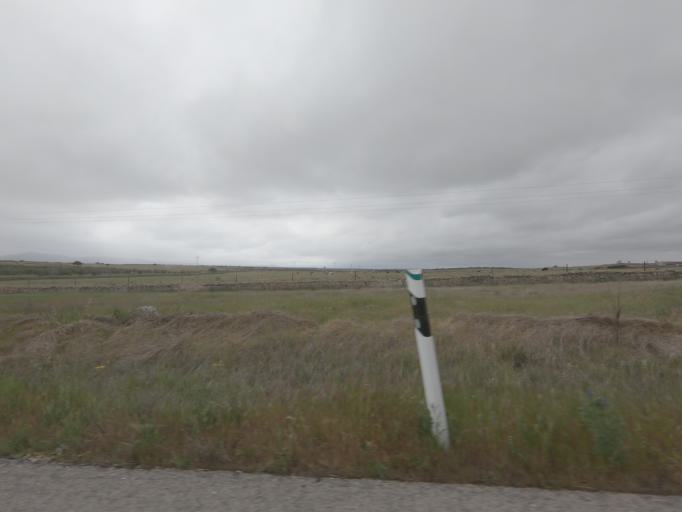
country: ES
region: Extremadura
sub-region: Provincia de Caceres
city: Malpartida de Caceres
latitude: 39.3726
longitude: -6.4541
